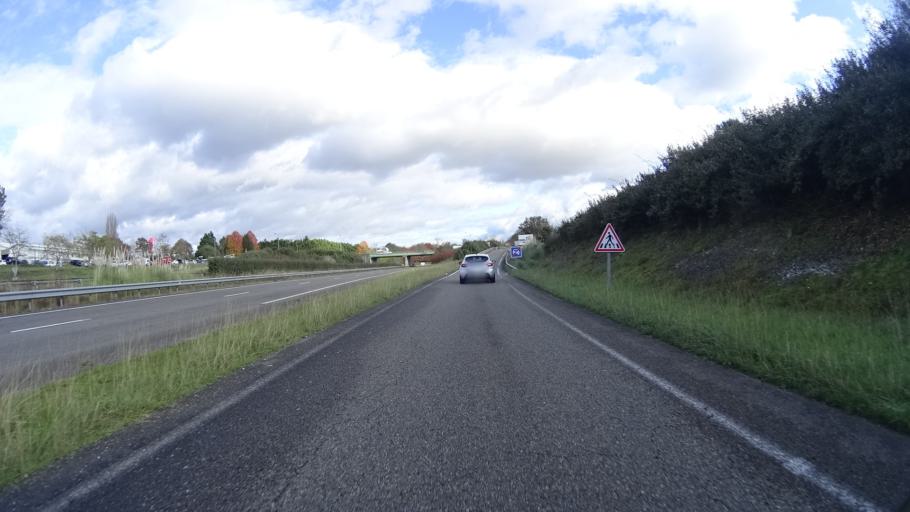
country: FR
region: Aquitaine
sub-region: Departement des Landes
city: Saint-Paul-les-Dax
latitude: 43.7444
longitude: -1.0575
